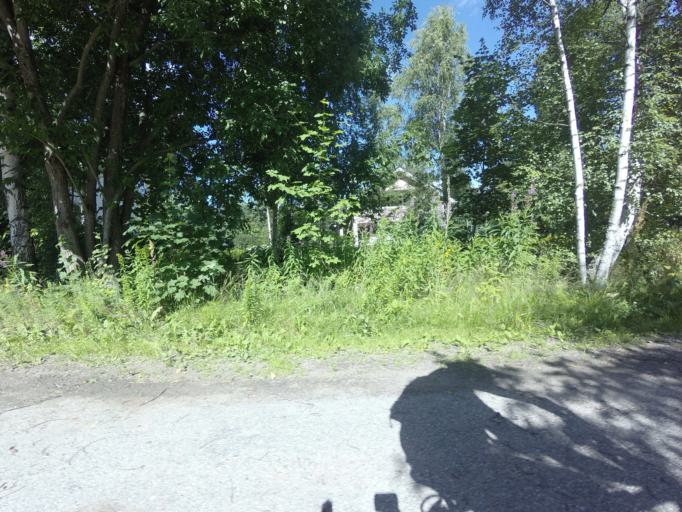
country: FI
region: Uusimaa
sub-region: Helsinki
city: Espoo
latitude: 60.1618
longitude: 24.6834
